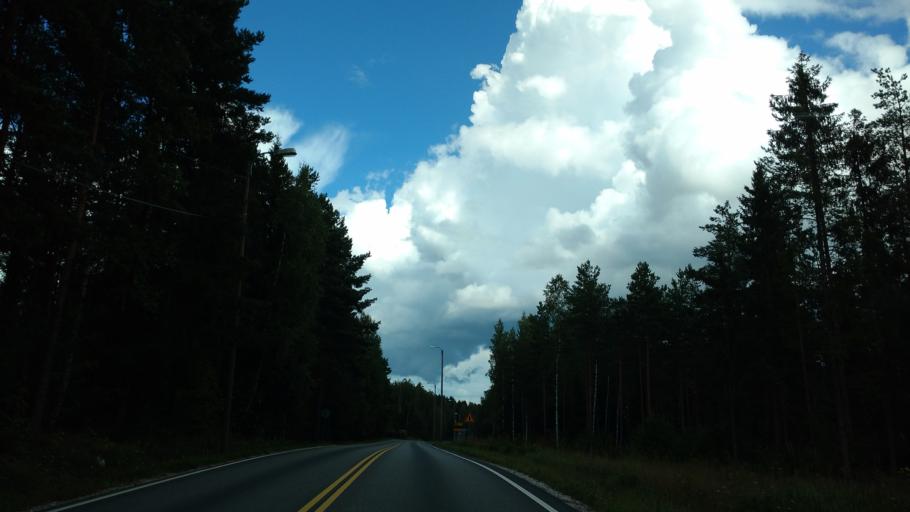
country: FI
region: Uusimaa
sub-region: Helsinki
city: Karjalohja
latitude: 60.2352
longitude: 23.7068
